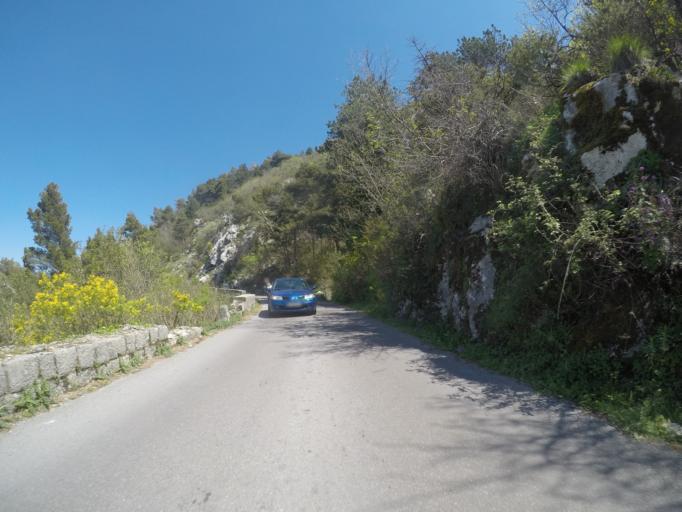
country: ME
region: Kotor
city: Kotor
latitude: 42.4079
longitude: 18.7779
